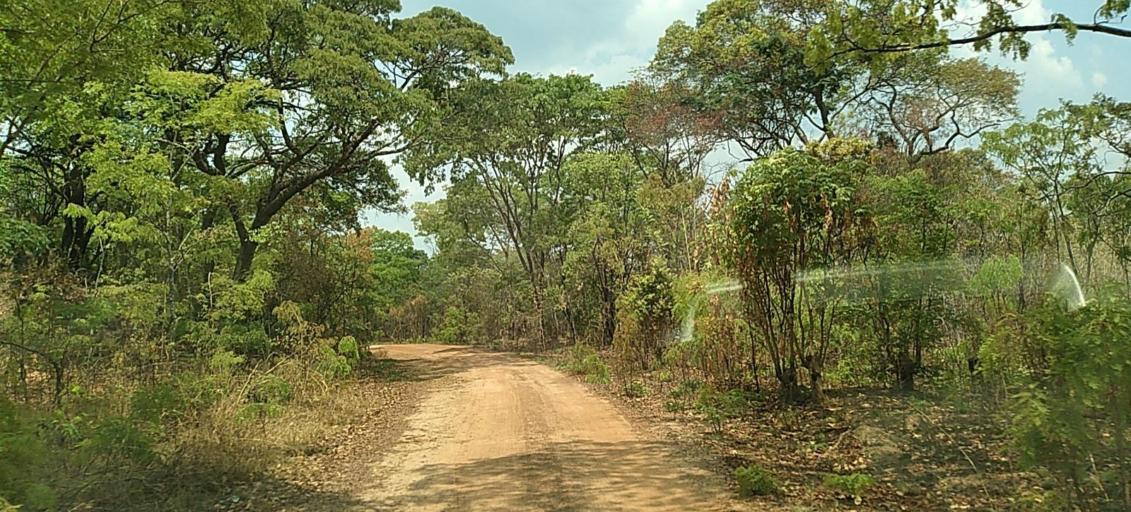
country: ZM
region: Copperbelt
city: Chingola
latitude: -12.7688
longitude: 27.7040
